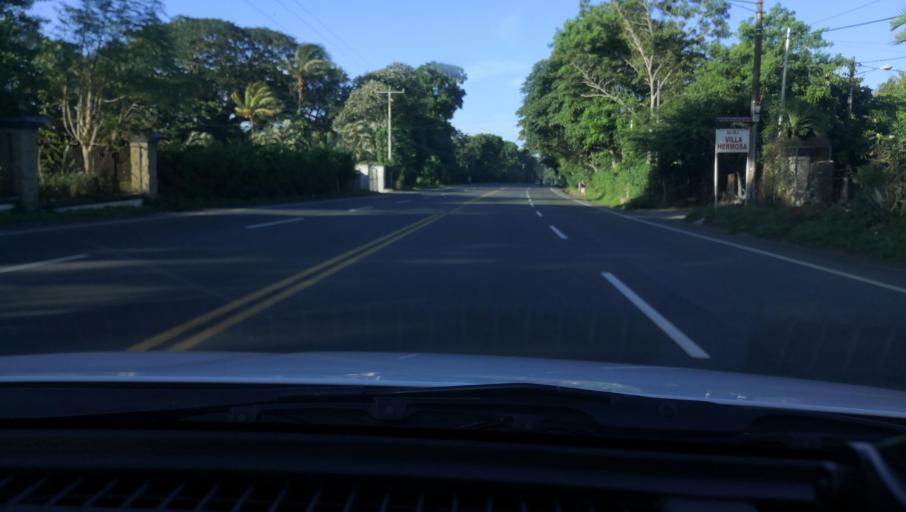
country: NI
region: Carazo
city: Diriamba
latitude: 11.8813
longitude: -86.2361
